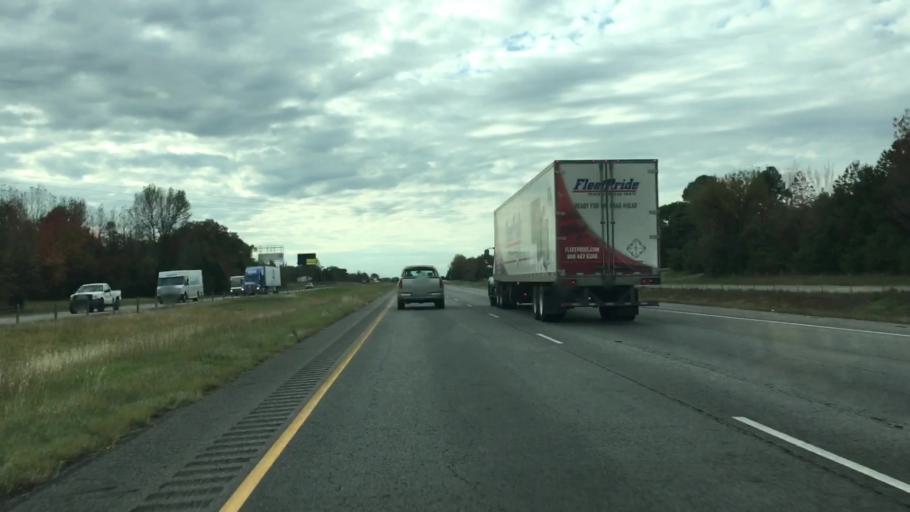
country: US
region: Arkansas
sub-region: Conway County
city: Morrilton
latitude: 35.1629
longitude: -92.6476
